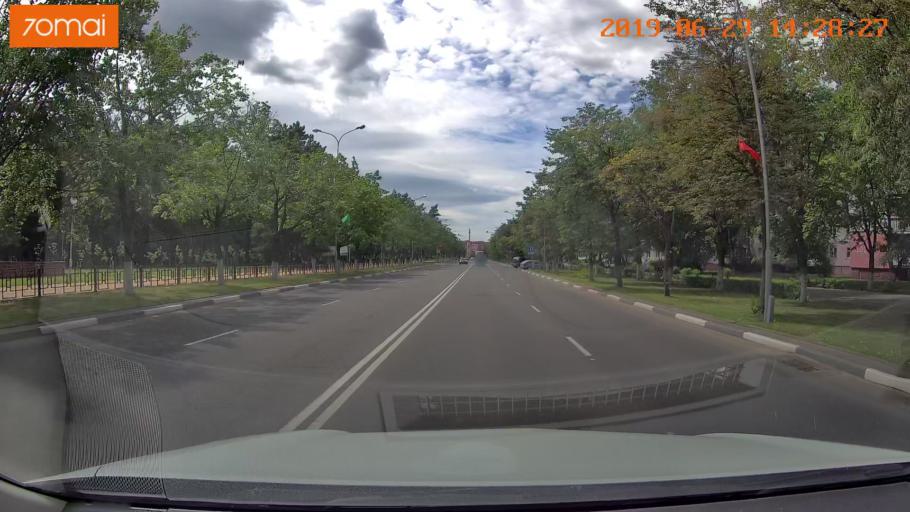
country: BY
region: Minsk
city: Salihorsk
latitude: 52.7831
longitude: 27.5321
